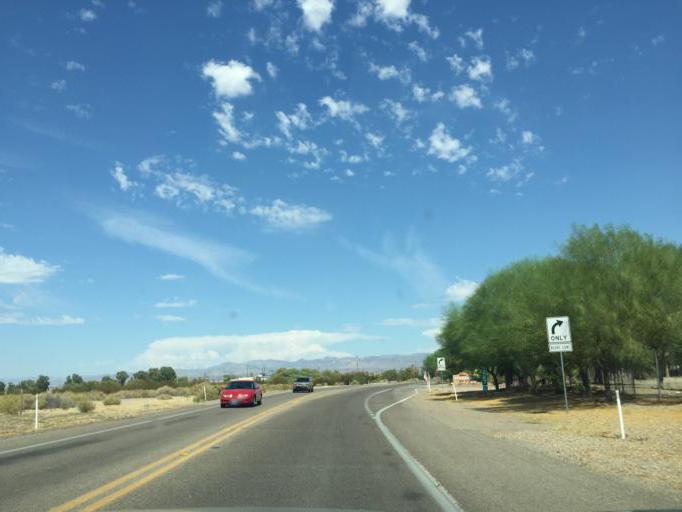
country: US
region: California
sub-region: San Bernardino County
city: Needles
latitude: 34.8628
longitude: -114.6016
